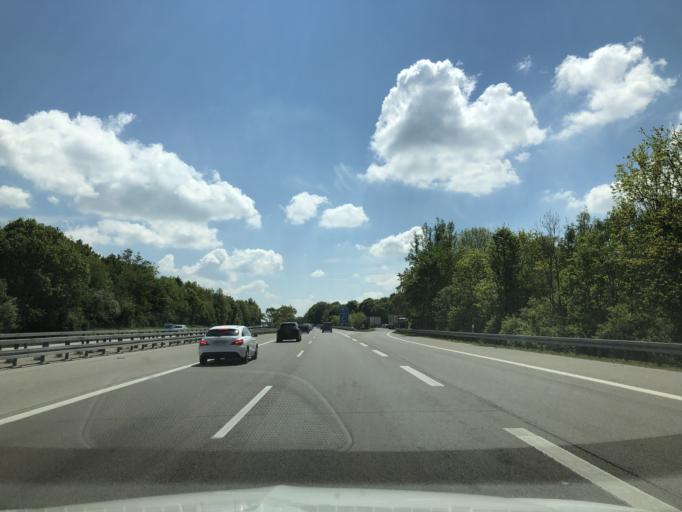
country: DE
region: Bavaria
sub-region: Upper Bavaria
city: Oberhaching
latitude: 48.0329
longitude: 11.6112
